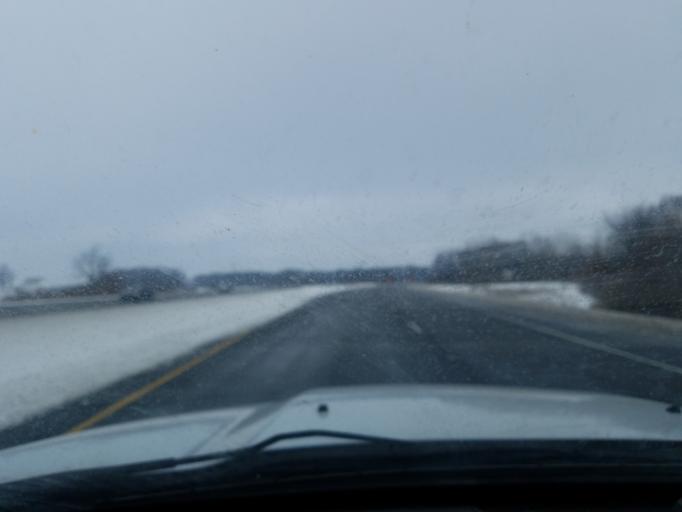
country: US
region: Indiana
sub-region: Marshall County
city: Argos
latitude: 41.2729
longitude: -86.2704
